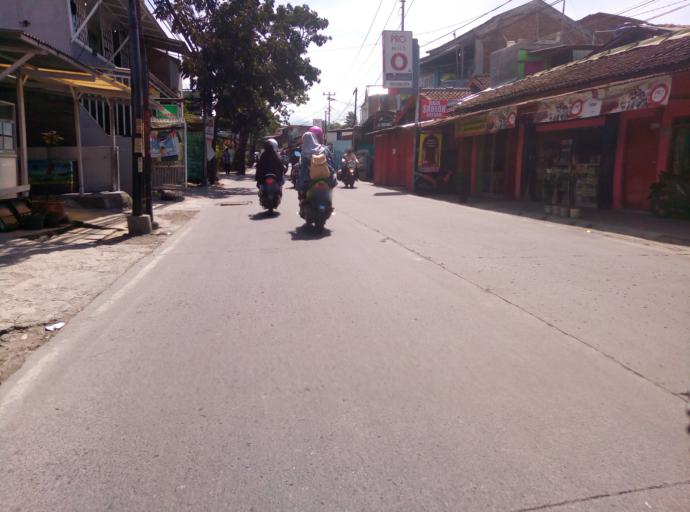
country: ID
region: West Java
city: Bandung
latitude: -6.8958
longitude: 107.6433
